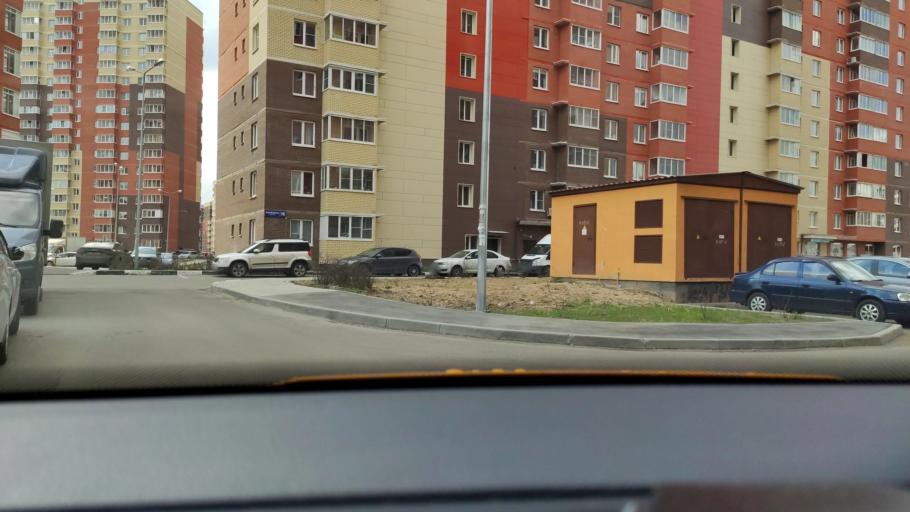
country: RU
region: Moskovskaya
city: Zheleznodorozhnyy
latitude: 55.7413
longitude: 38.0333
